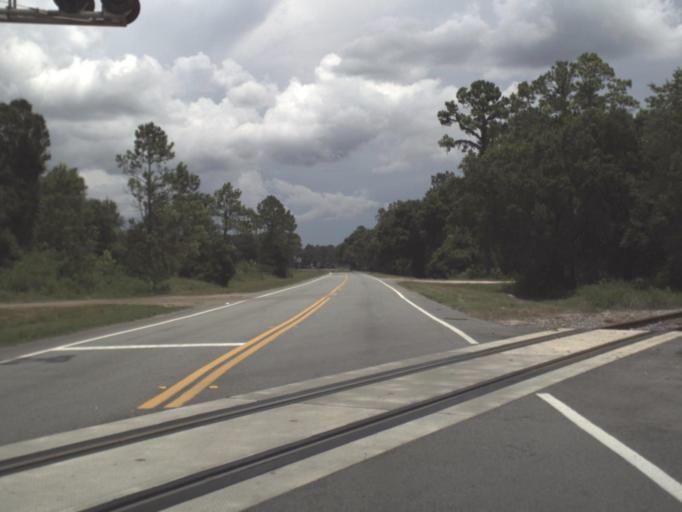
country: US
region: Florida
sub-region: Taylor County
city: Perry
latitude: 30.0853
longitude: -83.5273
